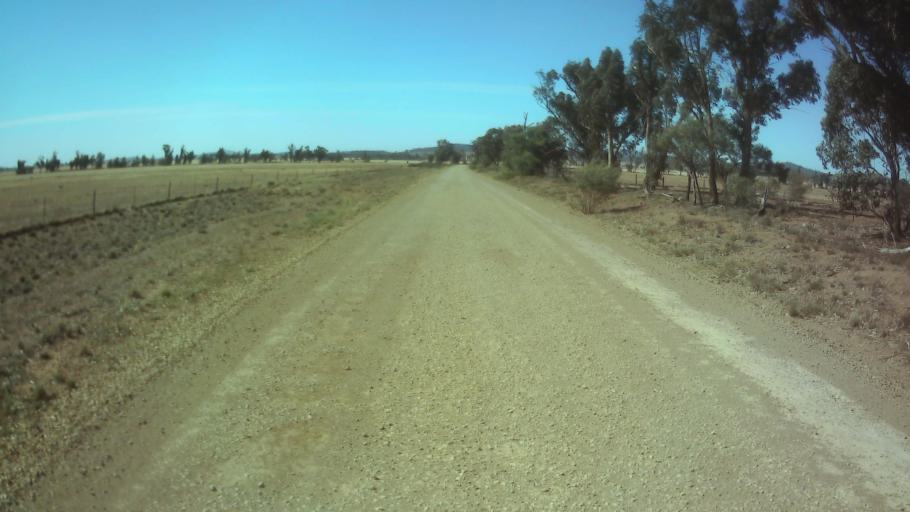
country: AU
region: New South Wales
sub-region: Forbes
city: Forbes
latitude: -33.7111
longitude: 147.7474
